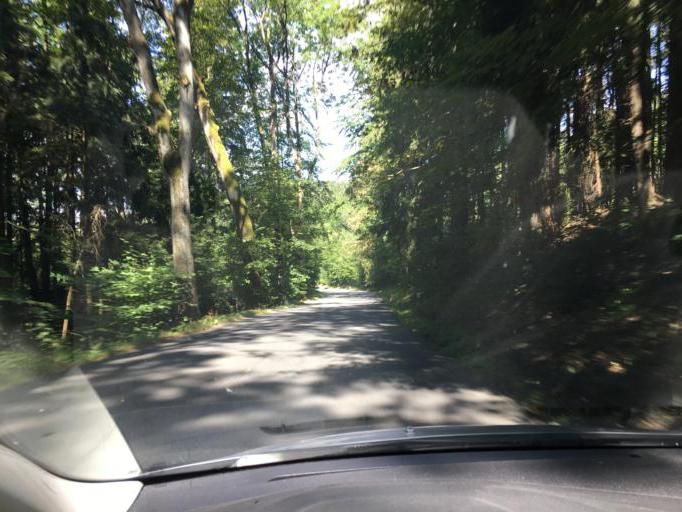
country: CZ
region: Liberecky
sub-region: Okres Semily
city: Vysoke nad Jizerou
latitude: 50.7063
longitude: 15.3764
